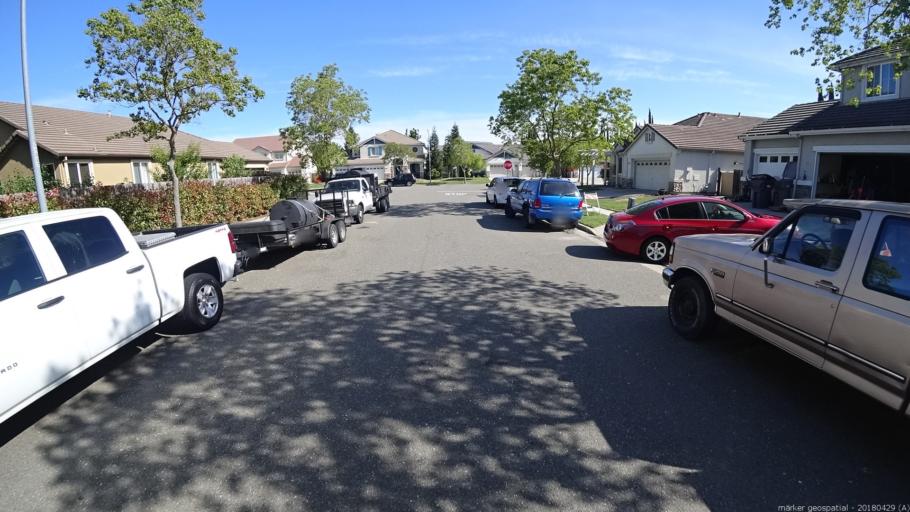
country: US
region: California
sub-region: Yolo County
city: West Sacramento
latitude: 38.5359
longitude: -121.5769
